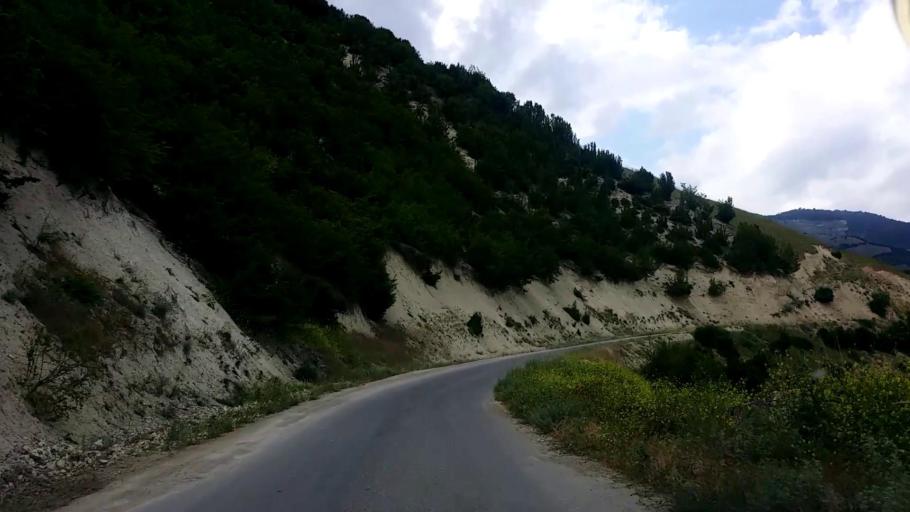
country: IR
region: Mazandaran
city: Chalus
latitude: 36.5403
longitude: 51.2729
